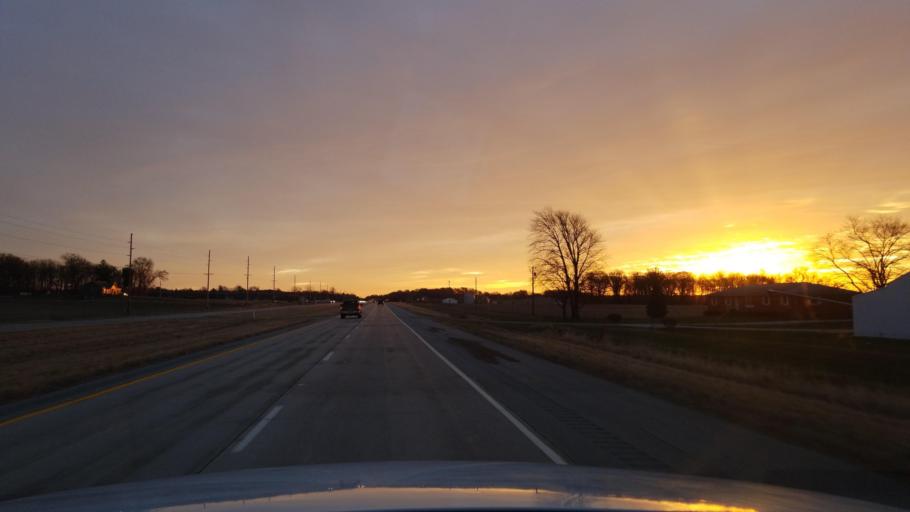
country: US
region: Indiana
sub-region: Posey County
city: Mount Vernon
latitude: 37.9420
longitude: -87.7681
